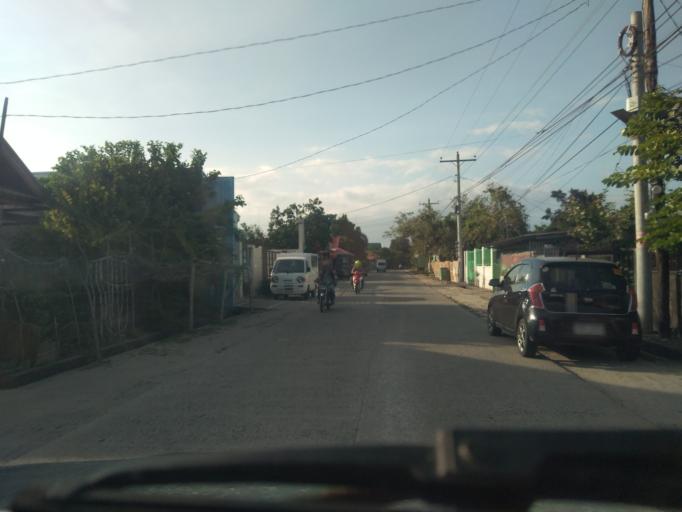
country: PH
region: Central Luzon
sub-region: Province of Pampanga
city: Bulaon
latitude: 15.0951
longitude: 120.6826
